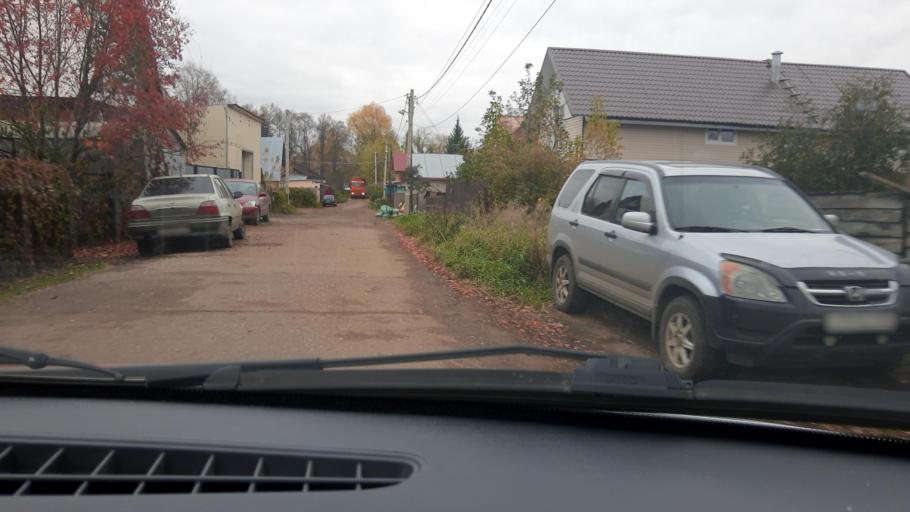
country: RU
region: Bashkortostan
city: Mikhaylovka
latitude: 54.7857
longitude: 55.8813
